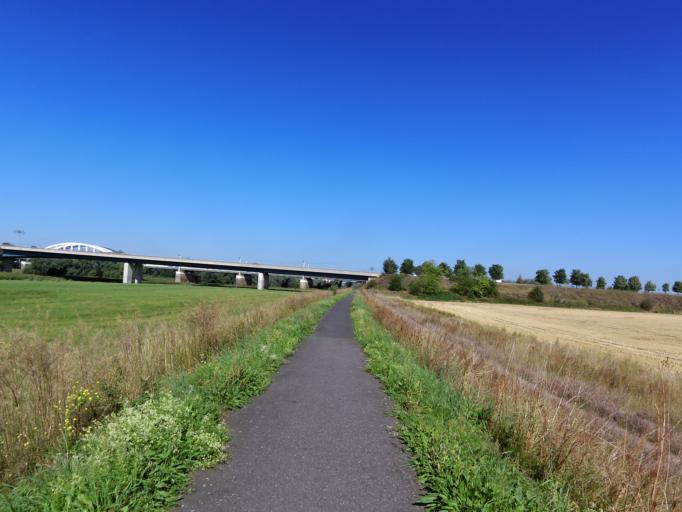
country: DE
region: Saxony
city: Riesa
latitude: 51.3108
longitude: 13.3005
